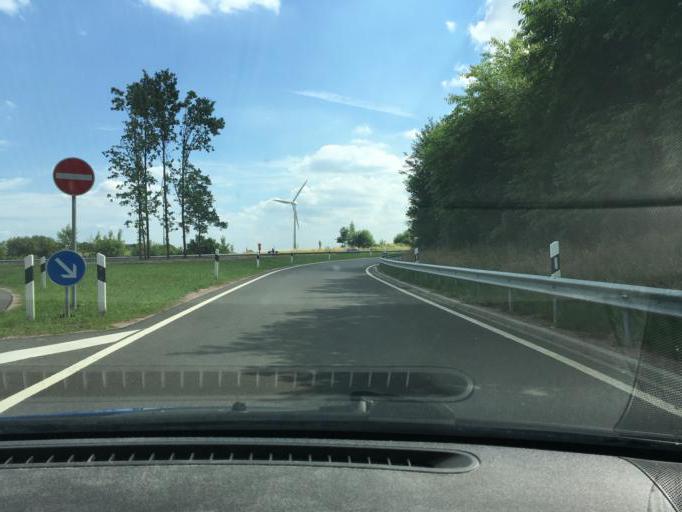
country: DE
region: Lower Saxony
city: Seevetal
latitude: 53.4015
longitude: 9.9013
